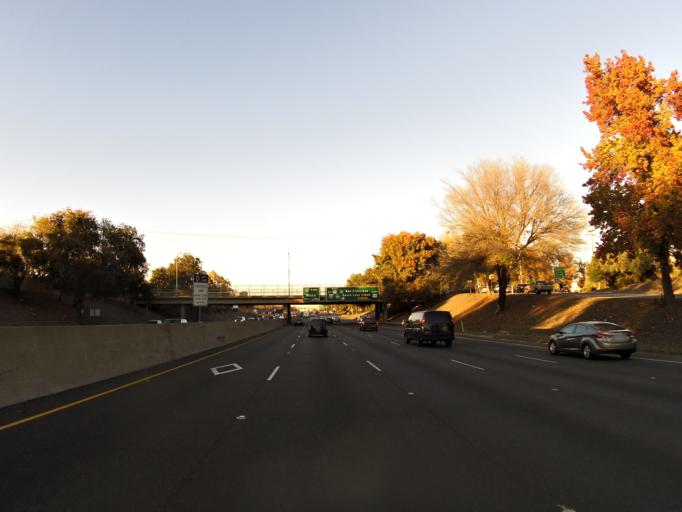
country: US
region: California
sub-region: Sacramento County
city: Sacramento
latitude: 38.5404
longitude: -121.4737
